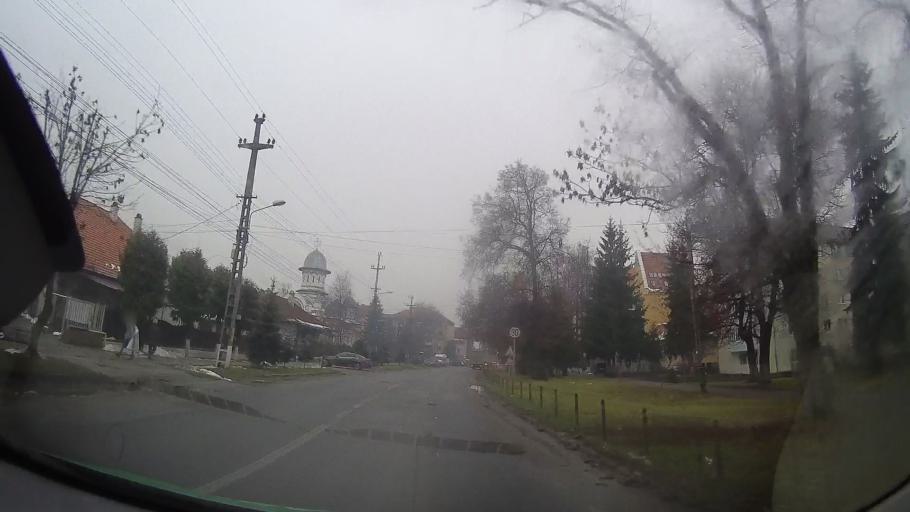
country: RO
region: Harghita
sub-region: Municipiul Gheorgheni
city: Gheorgheni
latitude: 46.7238
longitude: 25.6021
